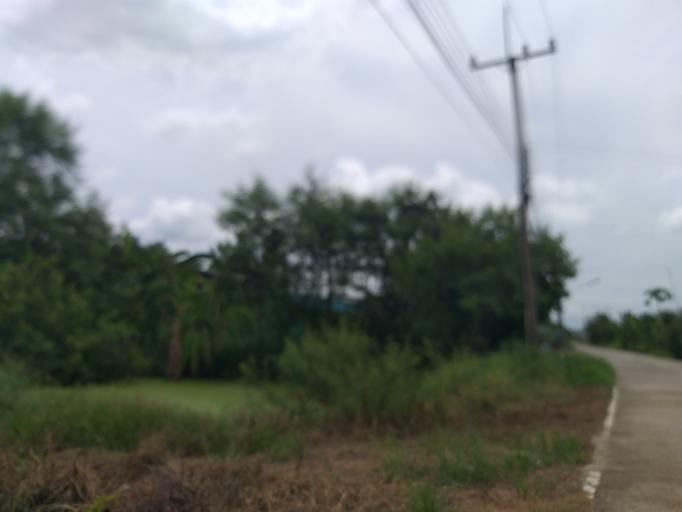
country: TH
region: Pathum Thani
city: Ban Lam Luk Ka
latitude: 13.9824
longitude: 100.8543
